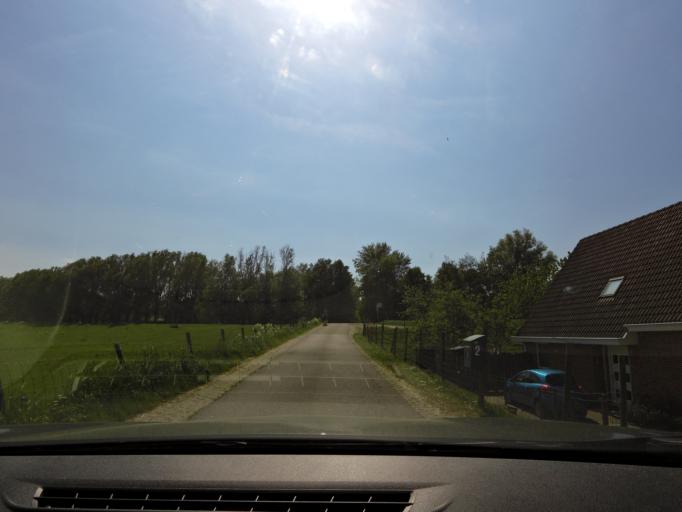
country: NL
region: South Holland
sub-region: Gemeente Binnenmaas
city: Heinenoord
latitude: 51.8375
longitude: 4.4613
